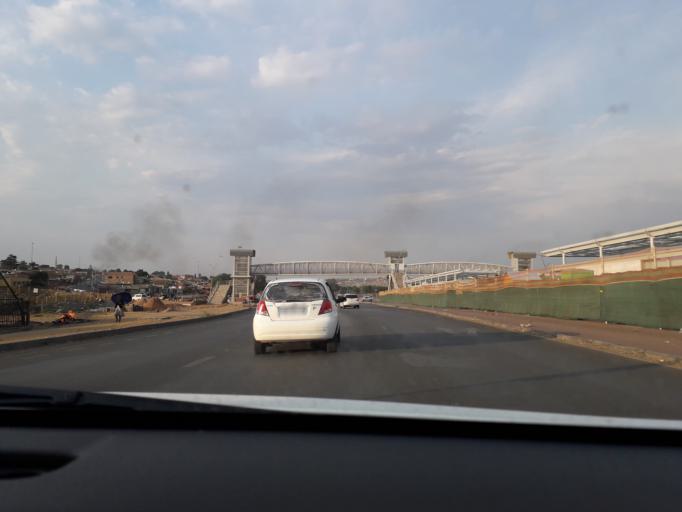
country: ZA
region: Gauteng
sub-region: Ekurhuleni Metropolitan Municipality
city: Tembisa
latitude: -26.0289
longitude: 28.1938
